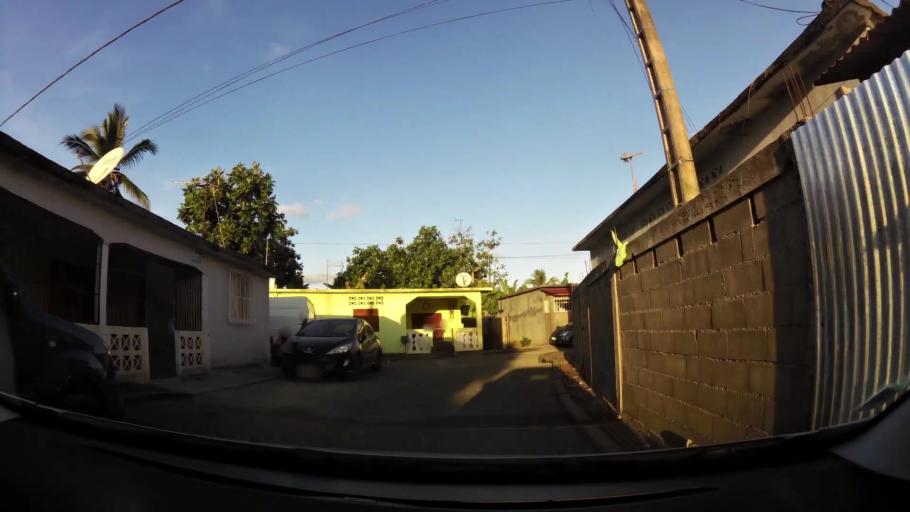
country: YT
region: Dembeni
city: Dembeni
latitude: -12.8436
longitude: 45.1920
